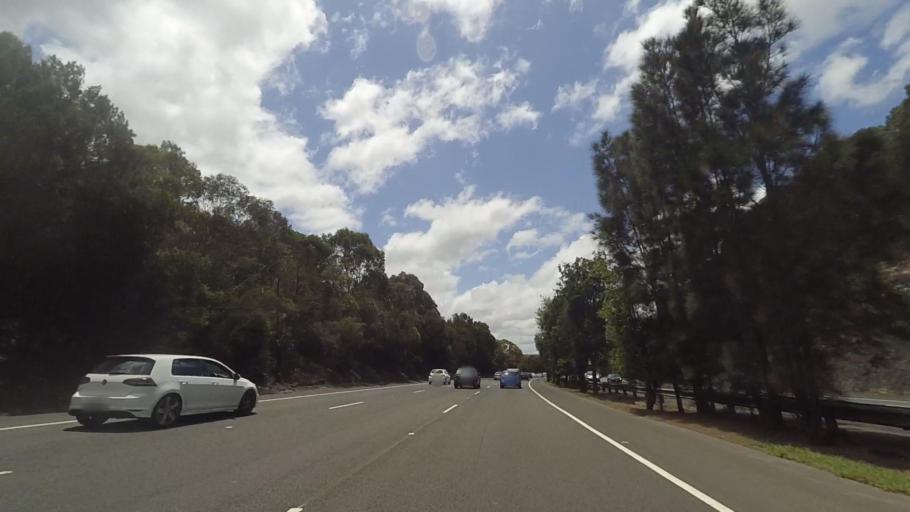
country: AU
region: New South Wales
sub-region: Ku-ring-gai
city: North Wahroonga
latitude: -33.6994
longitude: 151.1184
